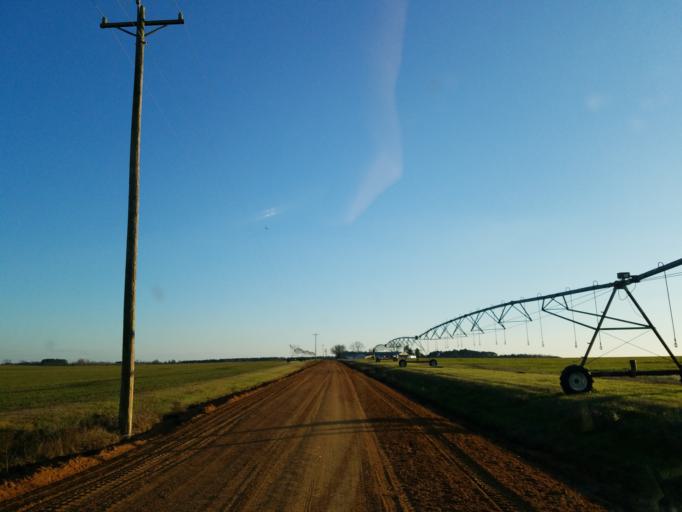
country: US
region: Georgia
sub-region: Worth County
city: Sylvester
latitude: 31.6074
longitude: -83.7868
